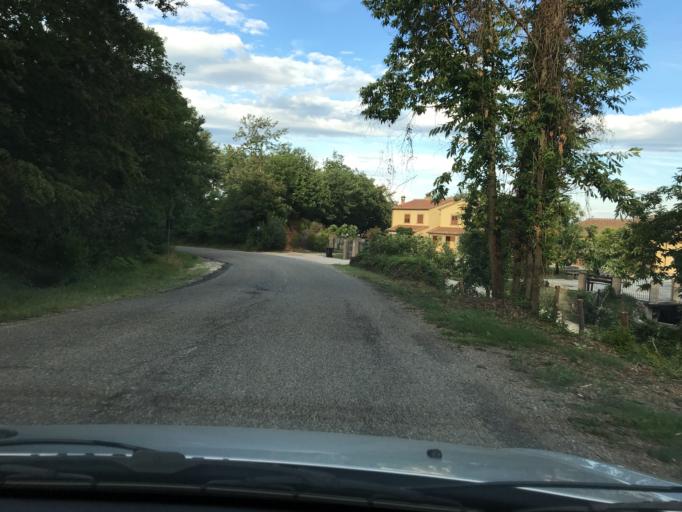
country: IT
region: Umbria
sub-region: Provincia di Terni
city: Guardea
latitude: 42.6478
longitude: 12.3565
